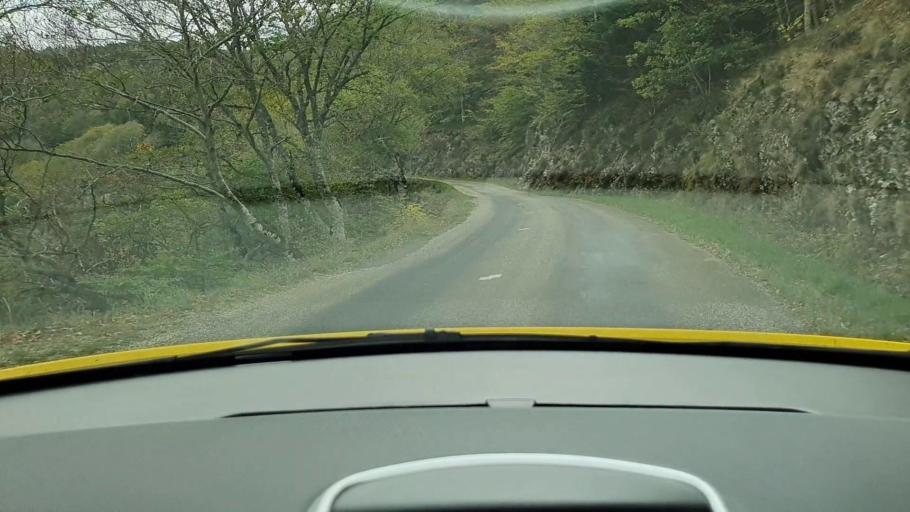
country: FR
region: Languedoc-Roussillon
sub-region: Departement de la Lozere
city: Meyrueis
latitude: 44.0831
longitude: 3.4202
